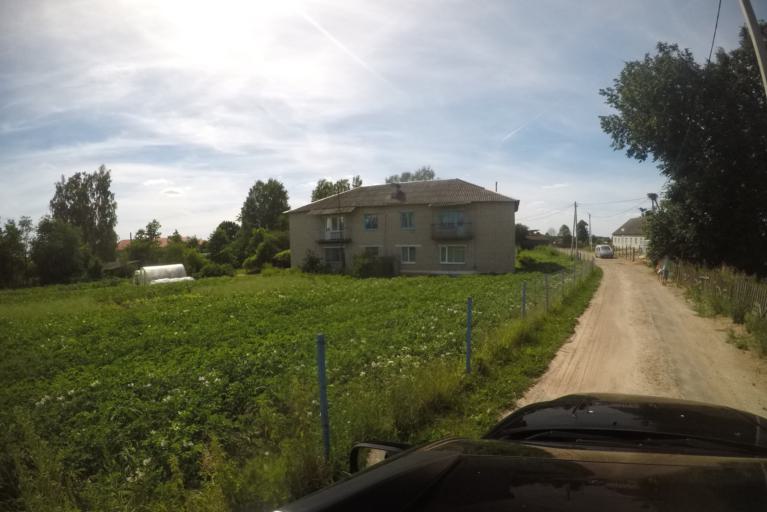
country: BY
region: Grodnenskaya
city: Hal'shany
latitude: 54.2574
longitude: 26.0182
